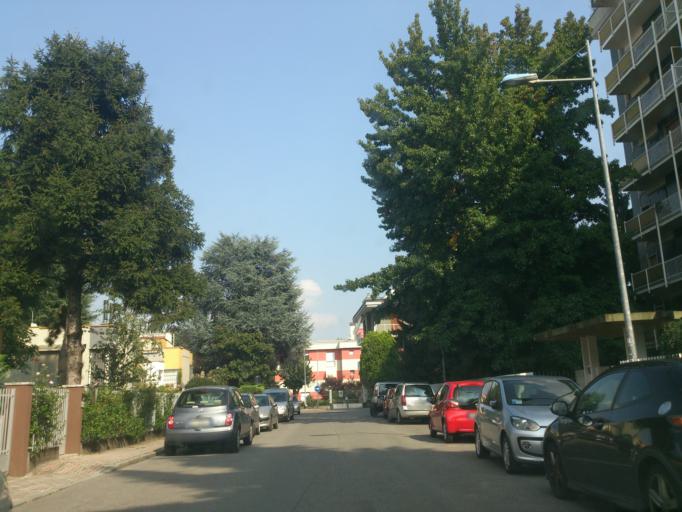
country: IT
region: Lombardy
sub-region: Citta metropolitana di Milano
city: San Donato Milanese
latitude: 45.4093
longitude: 9.2738
